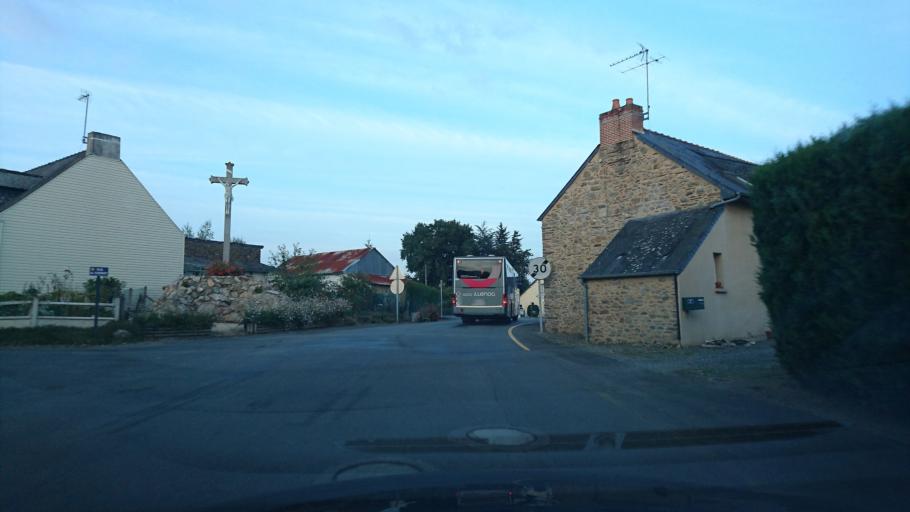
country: FR
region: Brittany
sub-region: Departement d'Ille-et-Vilaine
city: Maure-de-Bretagne
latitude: 47.8987
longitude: -1.9667
